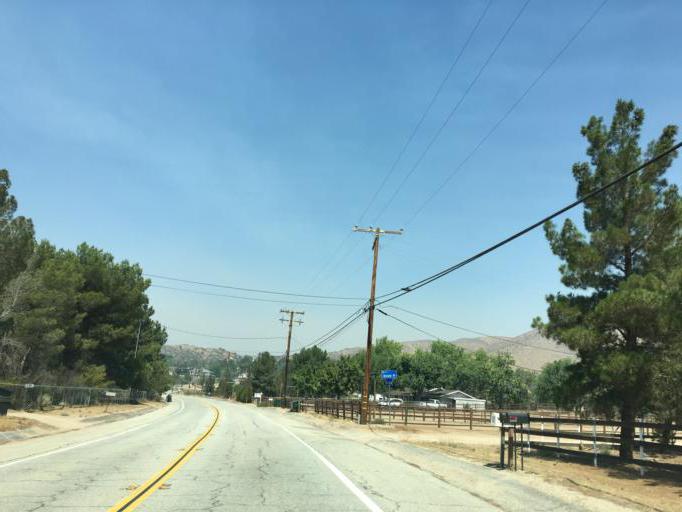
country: US
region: California
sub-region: Los Angeles County
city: Acton
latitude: 34.4745
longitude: -118.1669
